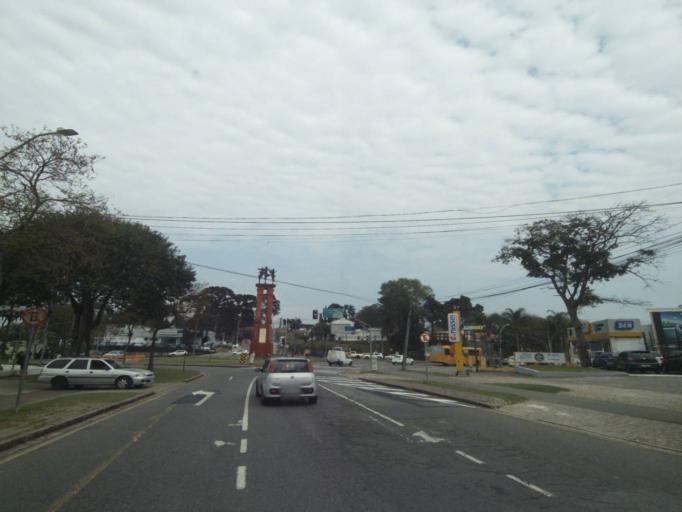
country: BR
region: Parana
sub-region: Curitiba
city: Curitiba
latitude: -25.4519
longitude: -49.3038
